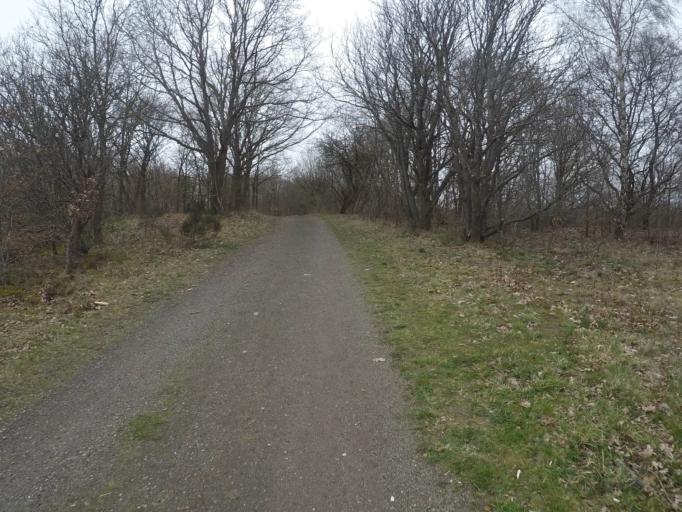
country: DE
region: Lower Saxony
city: Cuxhaven
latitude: 53.8363
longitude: 8.6457
